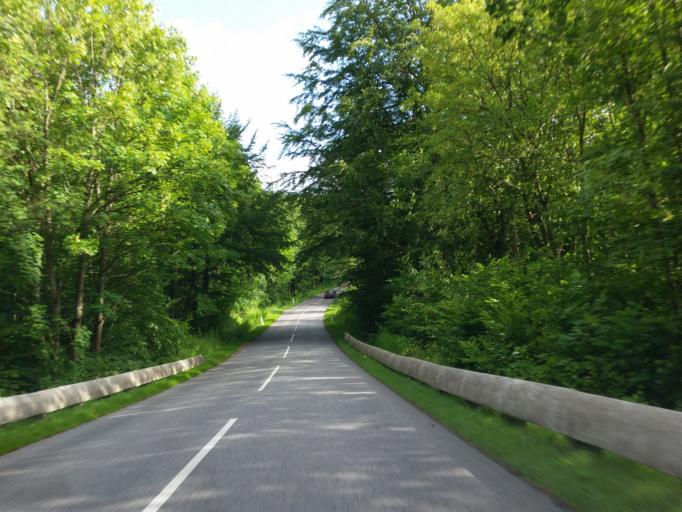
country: DK
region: South Denmark
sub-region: Vejle Kommune
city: Borkop
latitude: 55.6779
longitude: 9.6155
